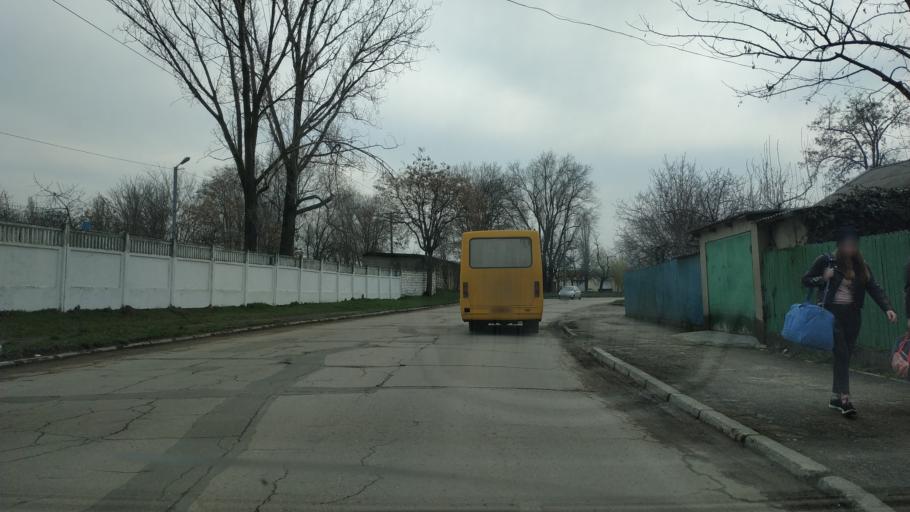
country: MD
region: Cahul
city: Cahul
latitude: 45.8933
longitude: 28.2005
